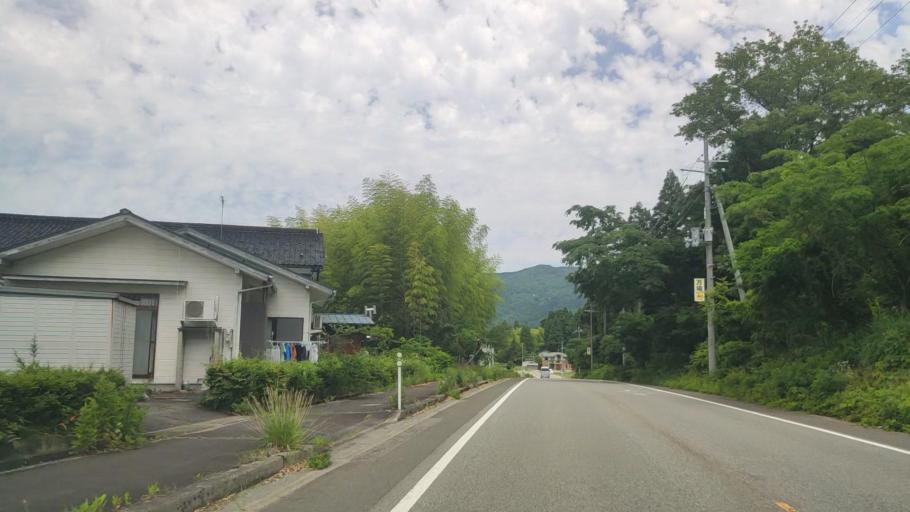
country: JP
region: Hyogo
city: Toyooka
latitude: 35.4999
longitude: 134.6735
